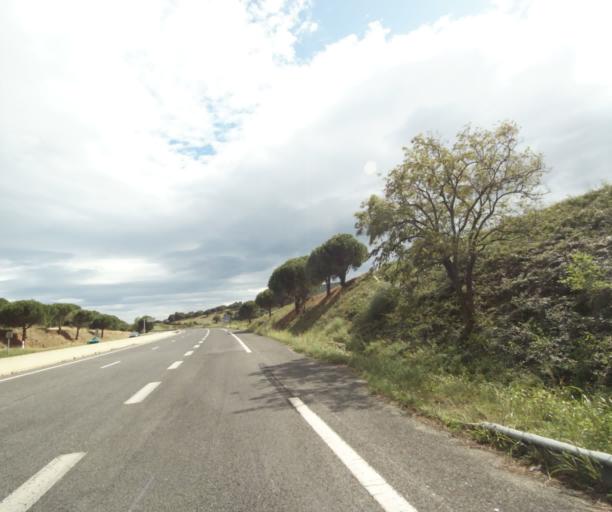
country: FR
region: Languedoc-Roussillon
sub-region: Departement des Pyrenees-Orientales
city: Argelers
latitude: 42.5360
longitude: 3.0329
